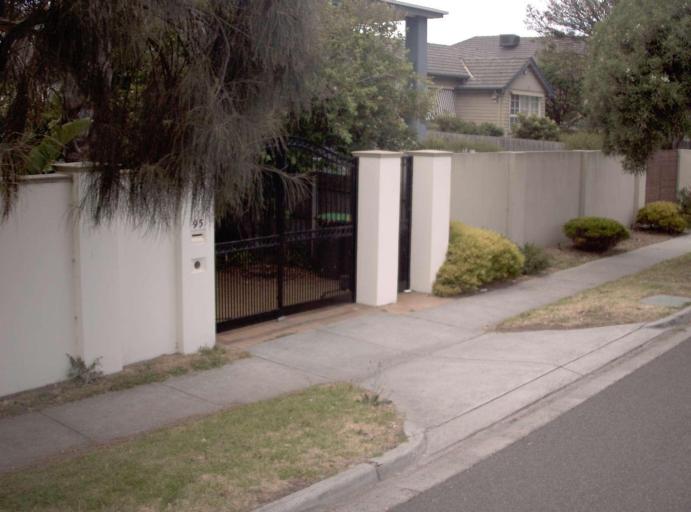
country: AU
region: Victoria
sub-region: Frankston
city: Seaford
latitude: -38.0990
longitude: 145.1258
